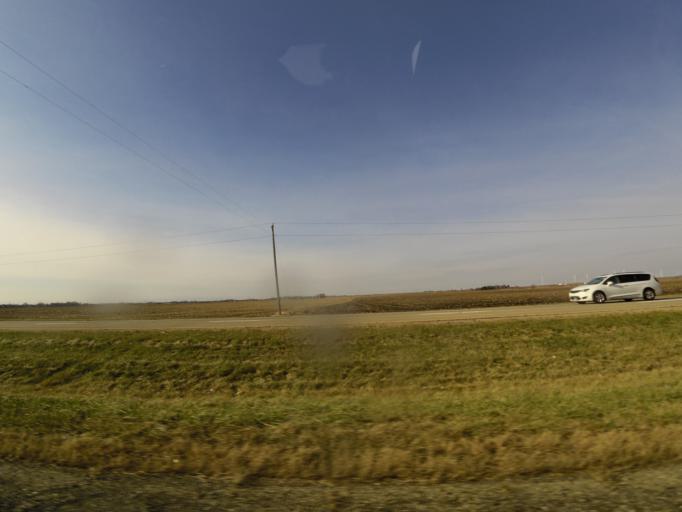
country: US
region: Illinois
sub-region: Macon County
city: Forsyth
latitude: 39.9458
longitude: -88.9554
